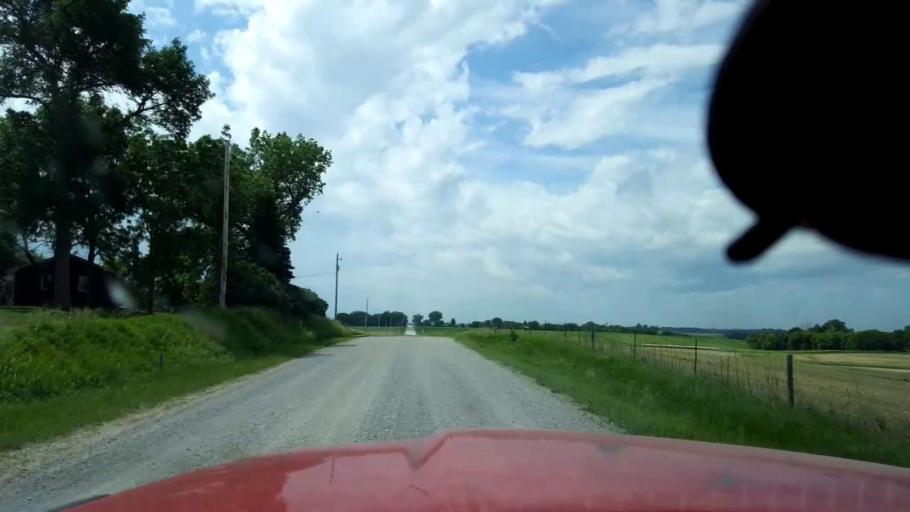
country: US
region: Iowa
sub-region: Cherokee County
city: Cherokee
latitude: 42.8182
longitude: -95.5343
